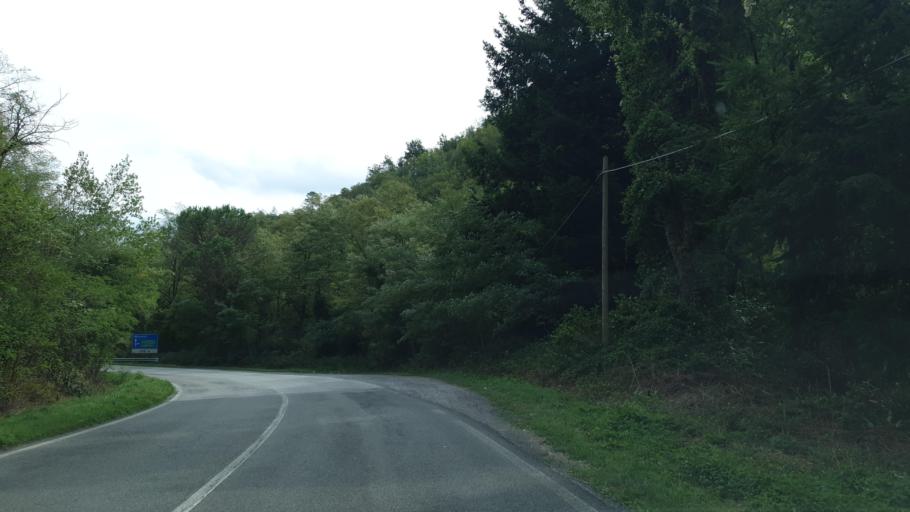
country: IT
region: Liguria
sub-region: Provincia di La Spezia
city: Carrodano
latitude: 44.2373
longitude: 9.6440
